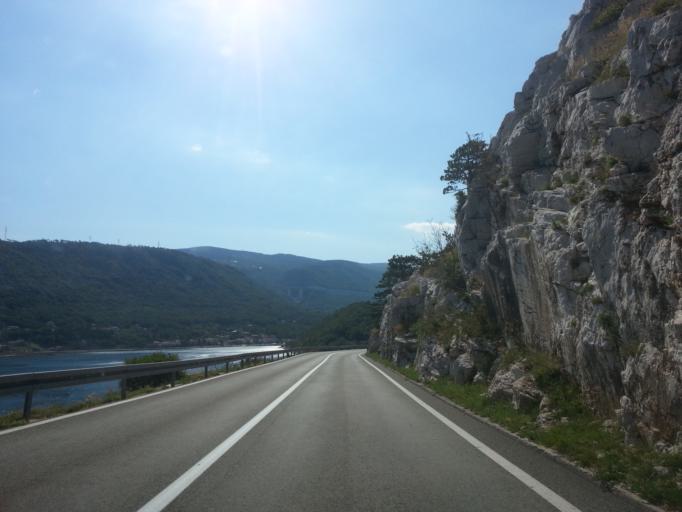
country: HR
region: Primorsko-Goranska
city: Kraljevica
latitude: 45.2817
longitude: 14.5692
